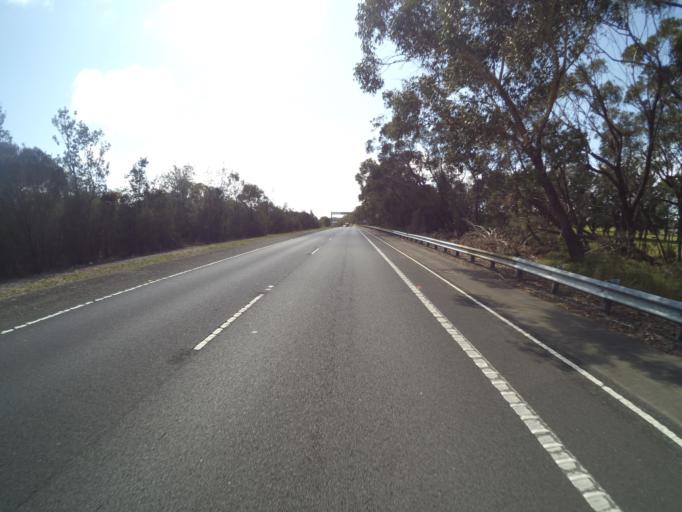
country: AU
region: New South Wales
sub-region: Wollongong
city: Helensburgh
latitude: -34.2458
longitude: 150.9395
